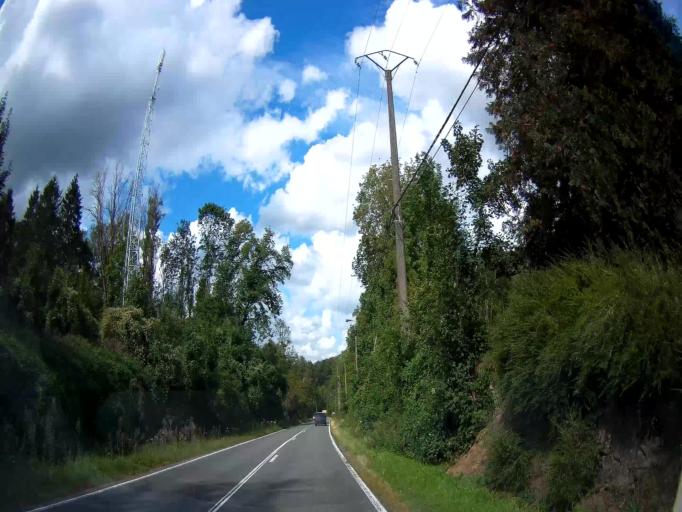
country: BE
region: Wallonia
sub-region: Province de Liege
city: Modave
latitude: 50.4479
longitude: 5.2935
